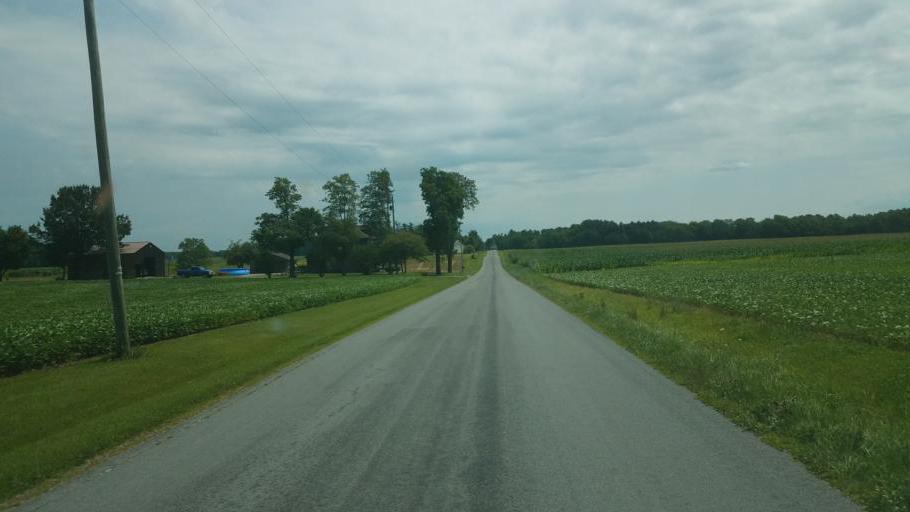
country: US
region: Ohio
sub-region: Wyandot County
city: Upper Sandusky
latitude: 40.8657
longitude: -83.2353
